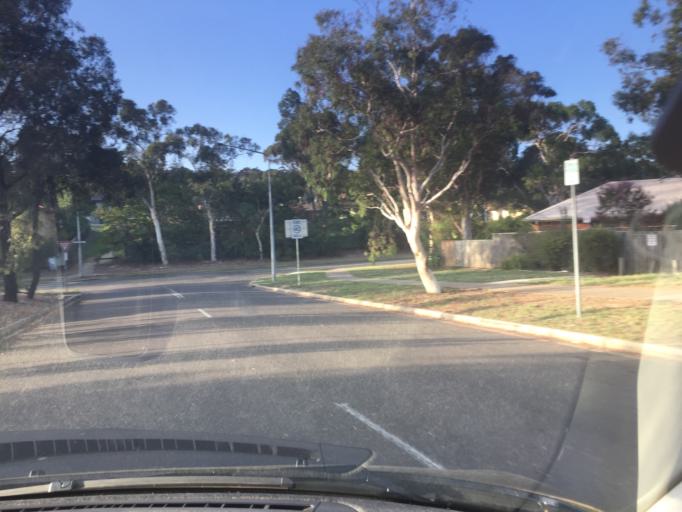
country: AU
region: Australian Capital Territory
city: Kaleen
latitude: -35.2197
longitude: 149.1037
